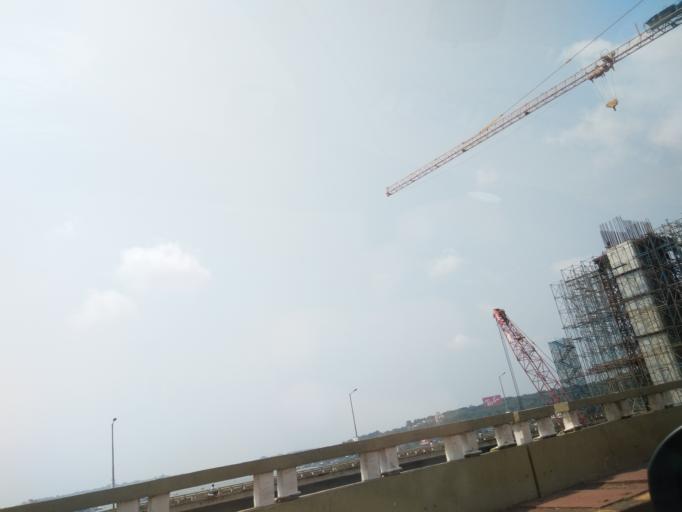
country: IN
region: Goa
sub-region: North Goa
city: Panaji
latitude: 15.5016
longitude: 73.8372
